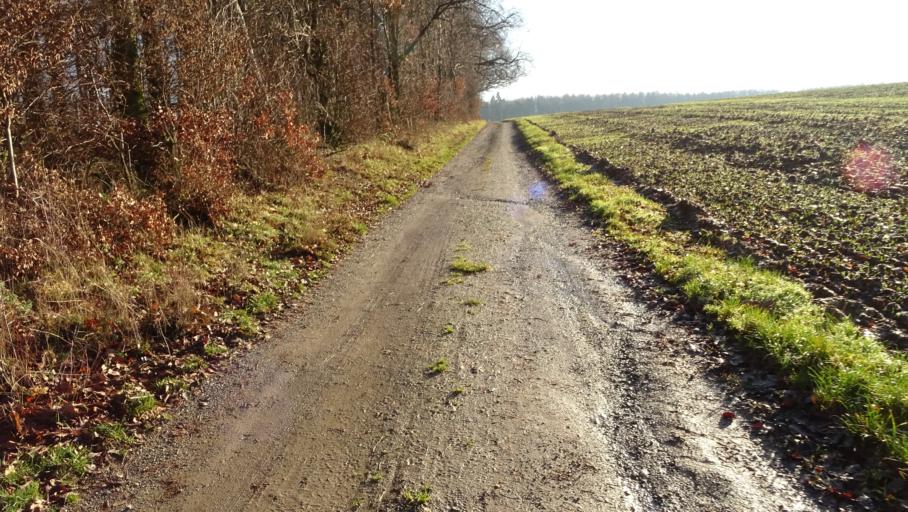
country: DE
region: Baden-Wuerttemberg
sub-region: Karlsruhe Region
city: Mosbach
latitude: 49.3470
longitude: 9.1952
